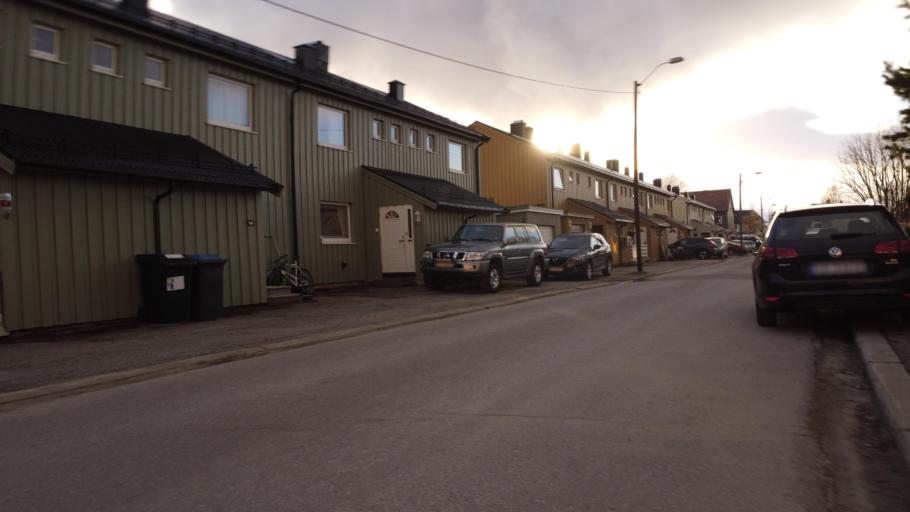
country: NO
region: Nordland
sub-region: Rana
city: Mo i Rana
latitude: 66.3154
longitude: 14.1596
